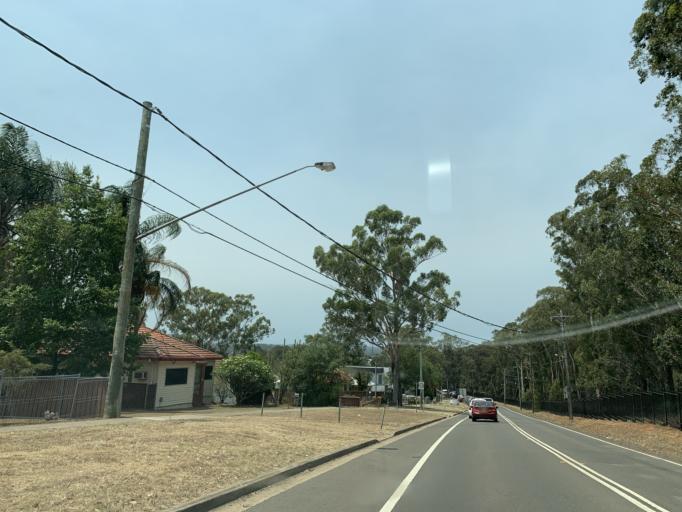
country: AU
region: New South Wales
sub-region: Blacktown
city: Blacktown
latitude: -33.7807
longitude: 150.9276
